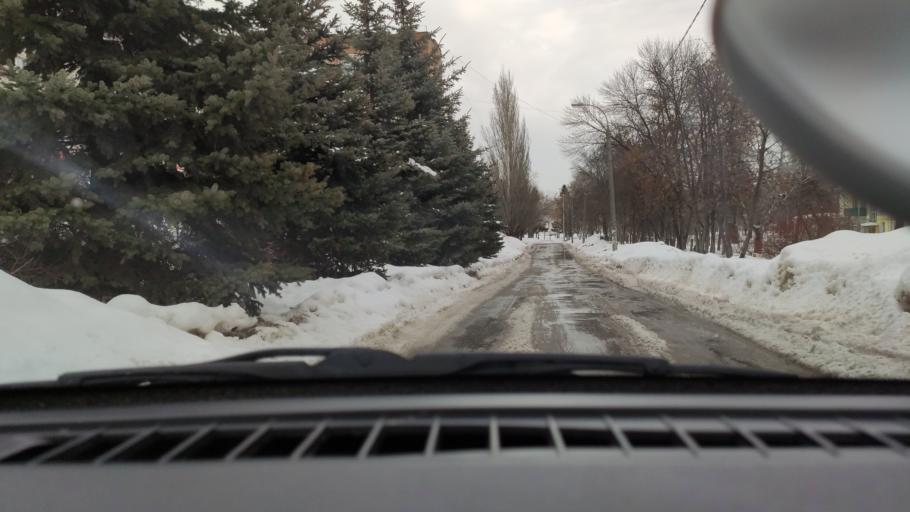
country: RU
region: Samara
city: Petra-Dubrava
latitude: 53.3033
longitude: 50.2738
